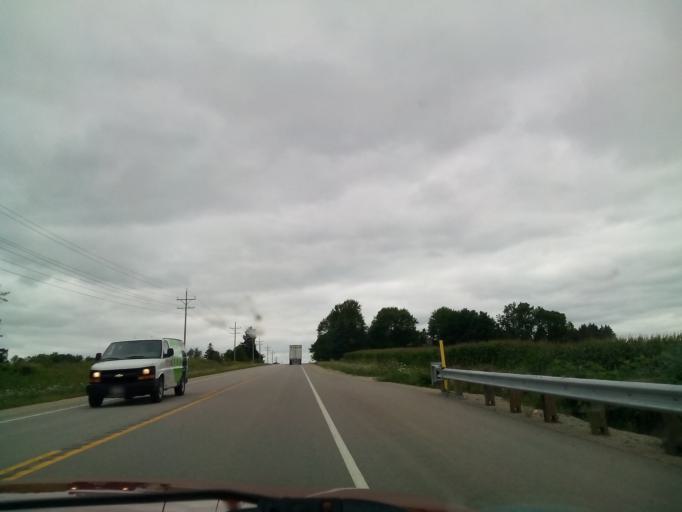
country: US
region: Wisconsin
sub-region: Outagamie County
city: Hortonville
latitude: 44.2723
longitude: -88.7028
